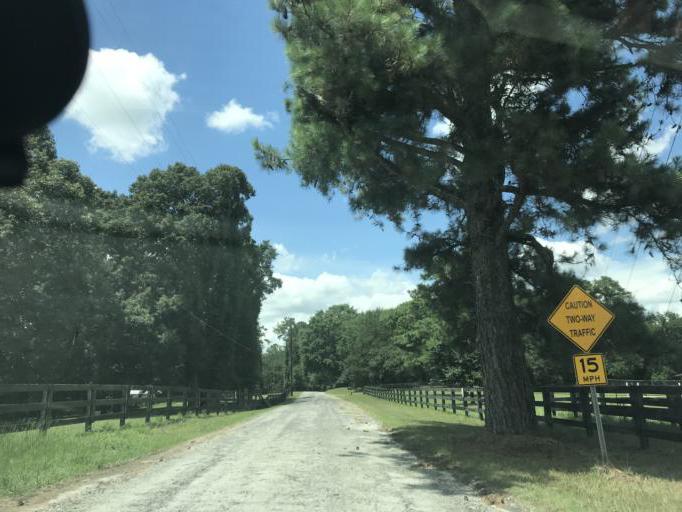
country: US
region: Georgia
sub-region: Gwinnett County
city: Suwanee
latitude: 34.0580
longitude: -84.1185
